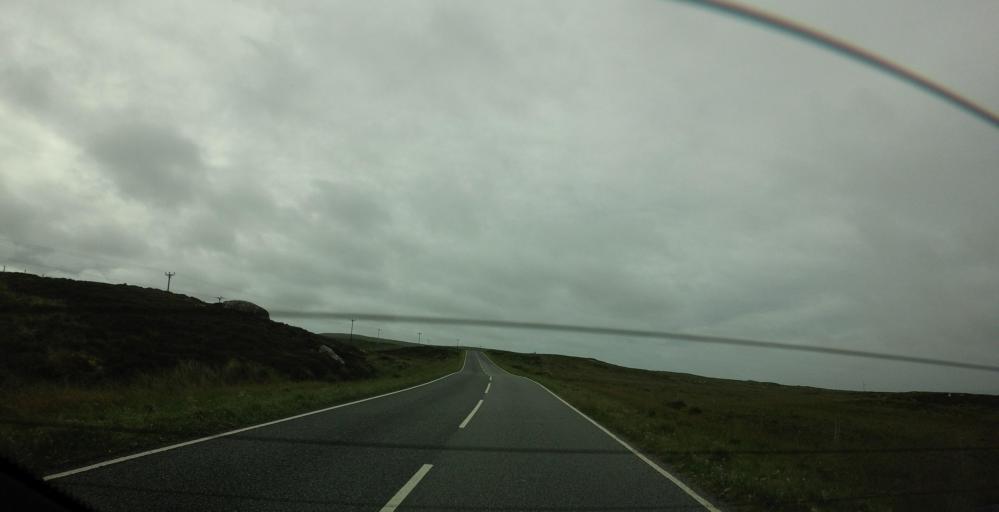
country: GB
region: Scotland
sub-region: Eilean Siar
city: Isle of South Uist
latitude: 57.2470
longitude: -7.3816
